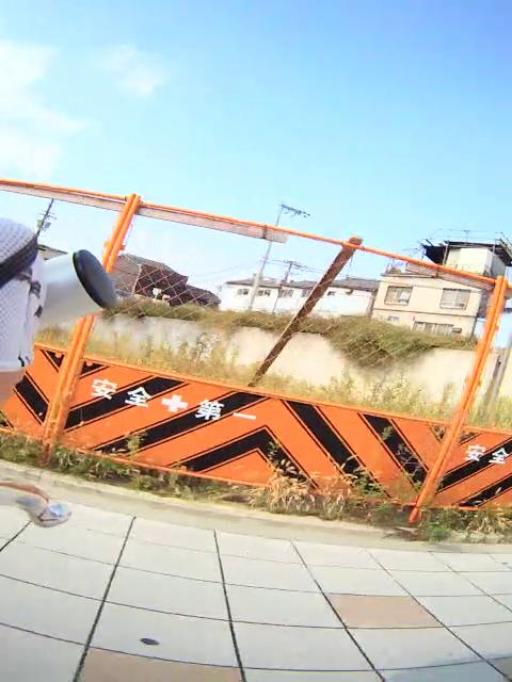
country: JP
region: Osaka
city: Suita
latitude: 34.7392
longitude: 135.4844
